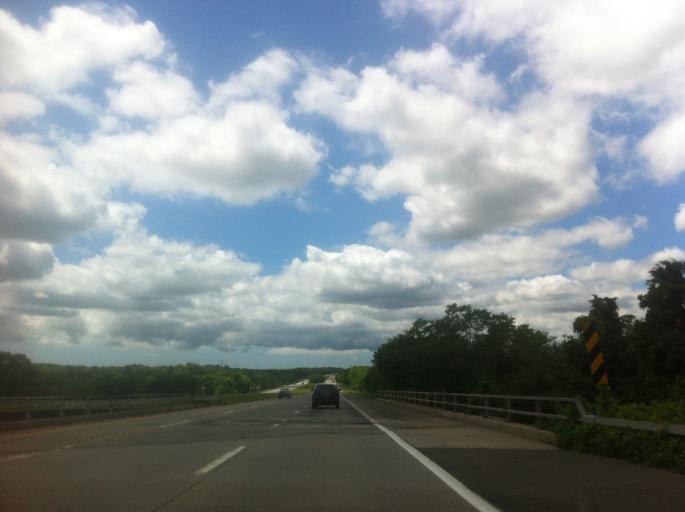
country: US
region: New York
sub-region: Suffolk County
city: Calverton
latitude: 40.9096
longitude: -72.7368
